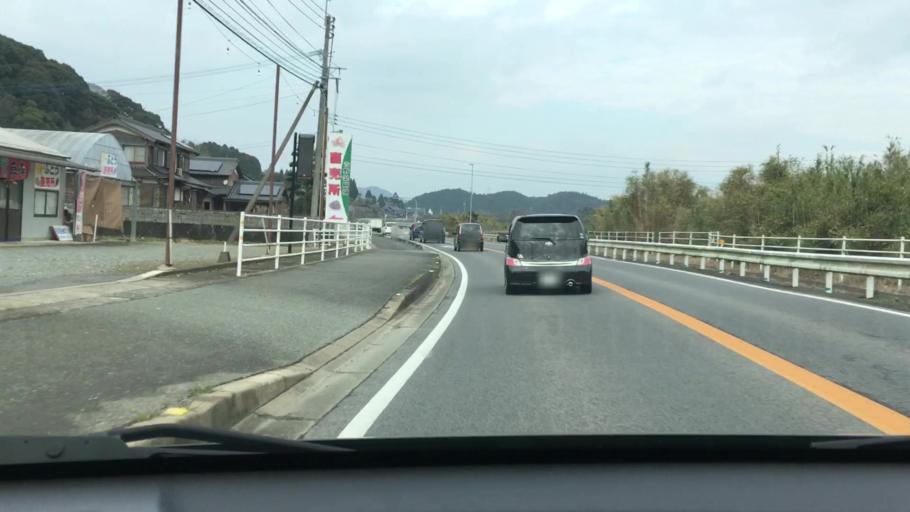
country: JP
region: Saga Prefecture
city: Imaricho-ko
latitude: 33.3265
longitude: 129.9298
